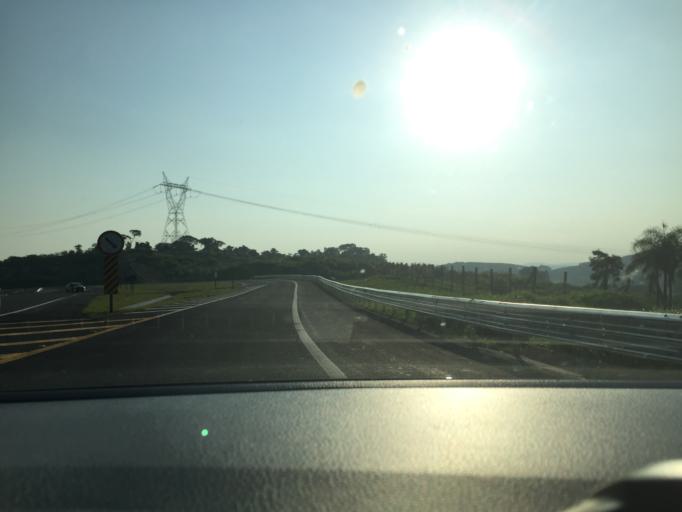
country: BR
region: Sao Paulo
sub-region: Louveira
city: Louveira
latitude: -23.0731
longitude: -46.9061
